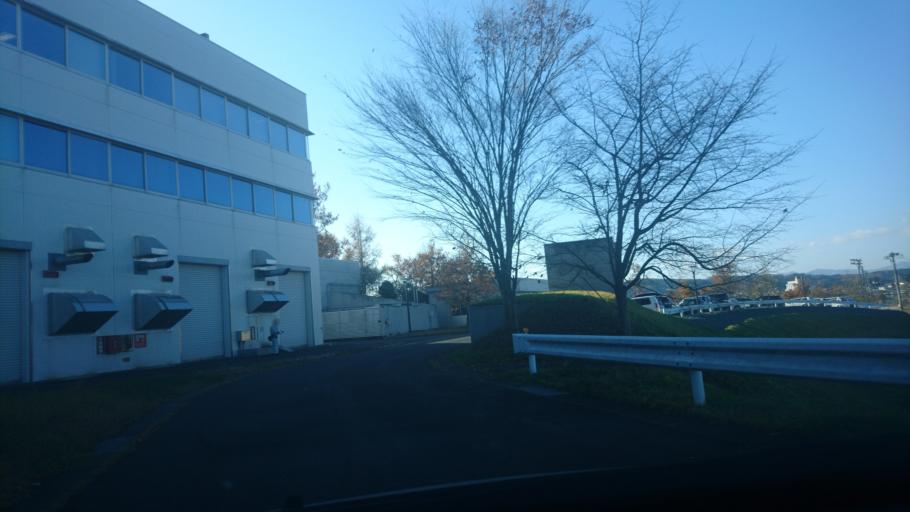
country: JP
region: Iwate
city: Ichinoseki
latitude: 38.9376
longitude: 141.1595
